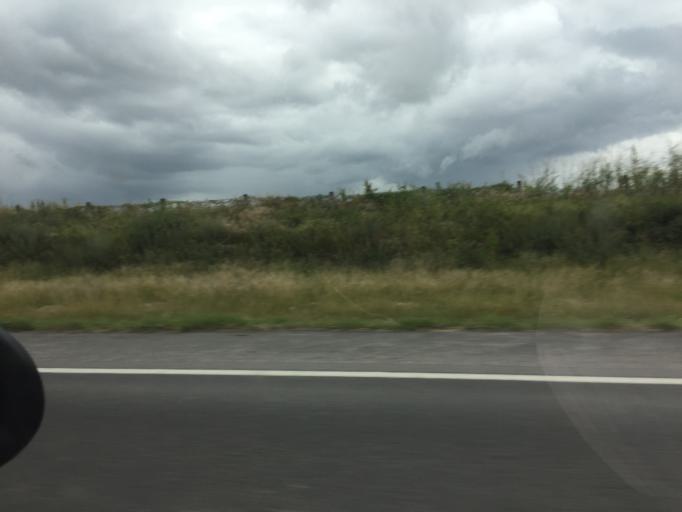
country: MX
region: Jalisco
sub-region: Zapotlanejo
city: La Mezquitera
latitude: 20.5727
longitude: -103.0852
